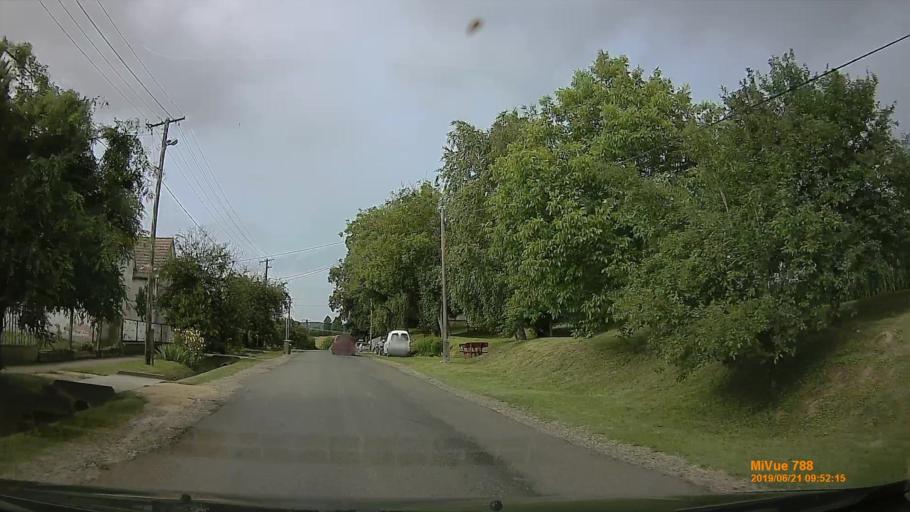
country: HU
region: Baranya
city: Sasd
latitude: 46.2447
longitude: 18.0168
